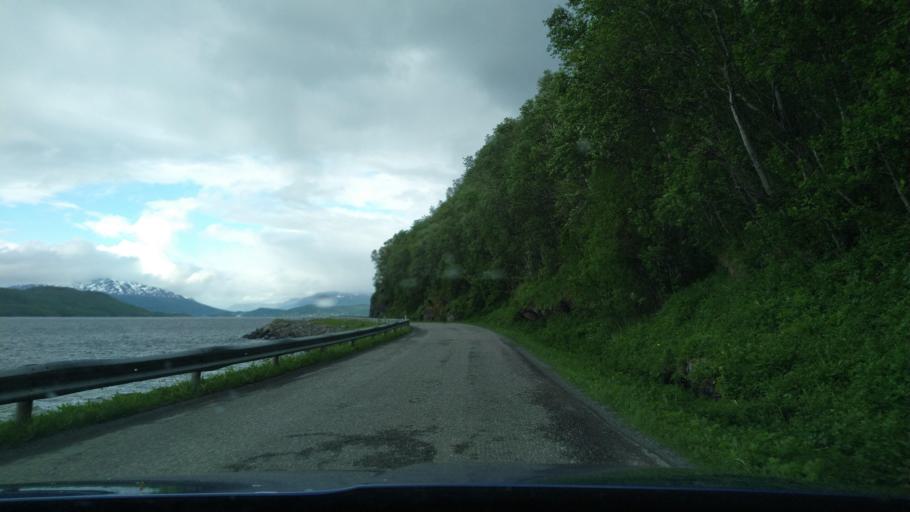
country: NO
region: Troms
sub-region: Lenvik
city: Finnsnes
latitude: 69.1431
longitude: 17.9198
